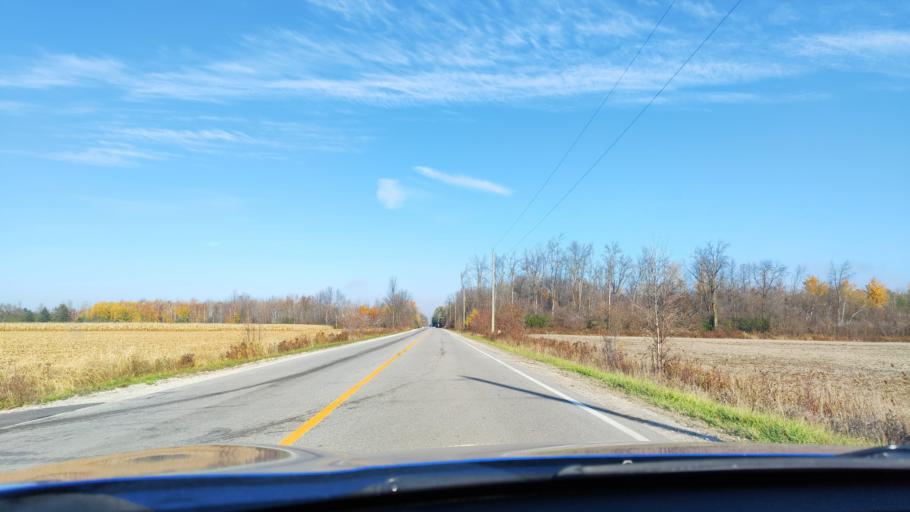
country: CA
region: Ontario
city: Wasaga Beach
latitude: 44.4021
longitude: -80.0582
